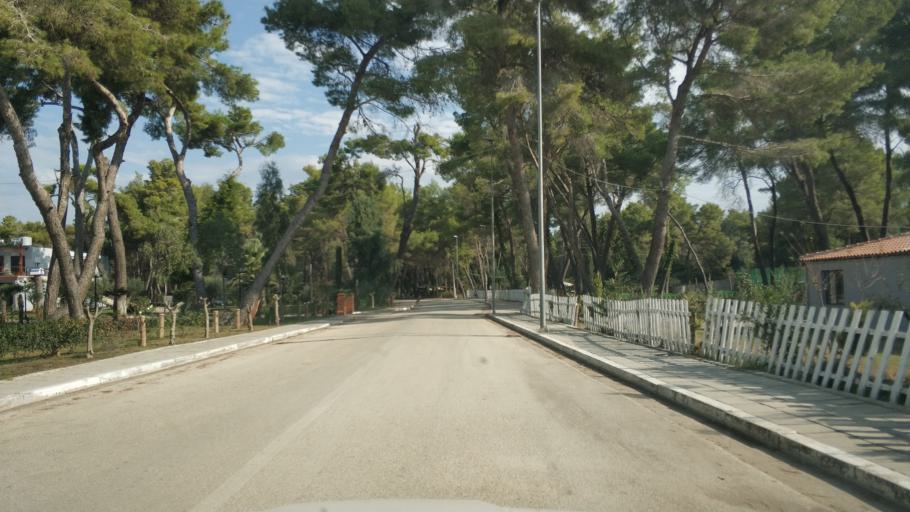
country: AL
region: Fier
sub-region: Rrethi i Lushnjes
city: Divjake
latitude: 40.9725
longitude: 19.4803
